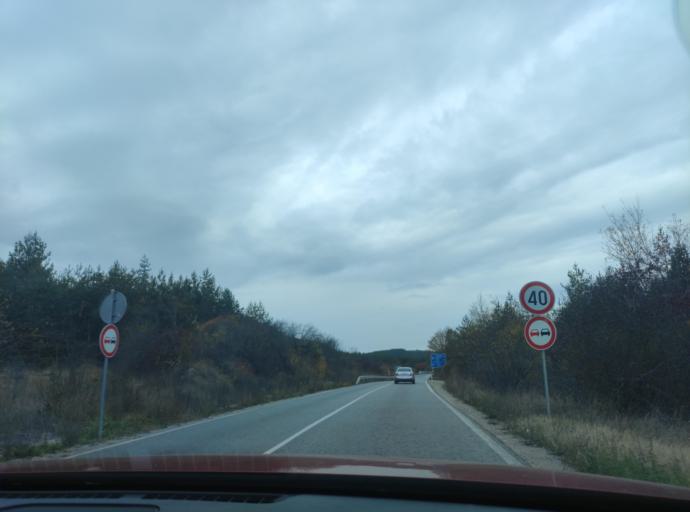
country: BG
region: Sofiya
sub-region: Obshtina Godech
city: Godech
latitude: 42.9807
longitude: 23.1321
